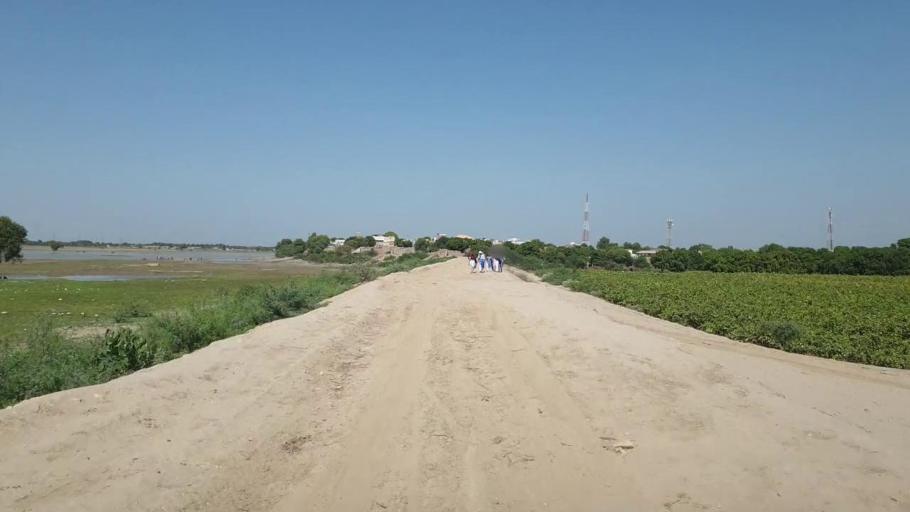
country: PK
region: Sindh
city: Matiari
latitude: 25.6453
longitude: 68.4932
